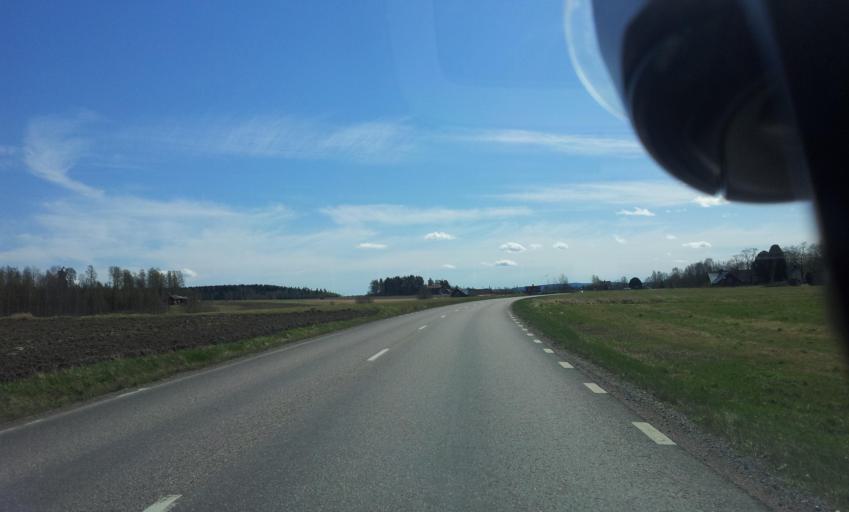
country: SE
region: Dalarna
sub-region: Borlange Kommun
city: Ornas
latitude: 60.4765
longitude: 15.5017
